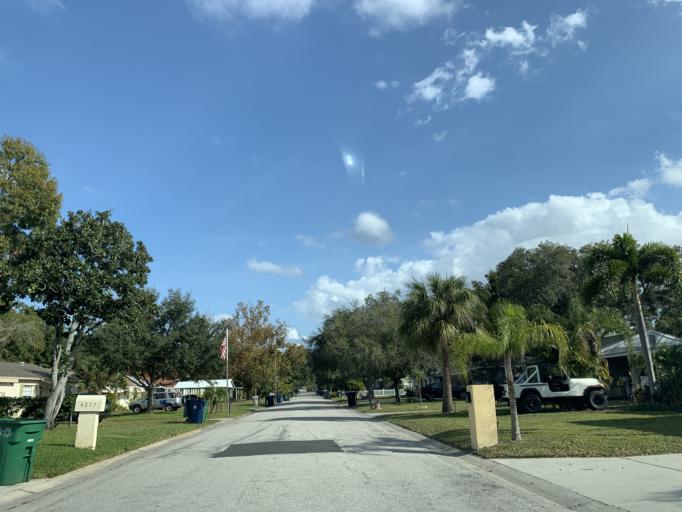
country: US
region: Florida
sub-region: Hillsborough County
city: Tampa
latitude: 27.9058
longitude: -82.5157
